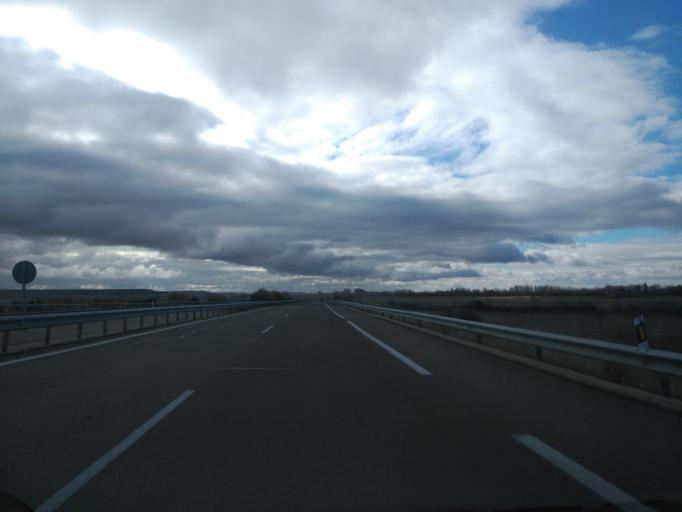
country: ES
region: Castille and Leon
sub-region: Provincia de Palencia
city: Fromista
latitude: 42.2461
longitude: -4.4200
